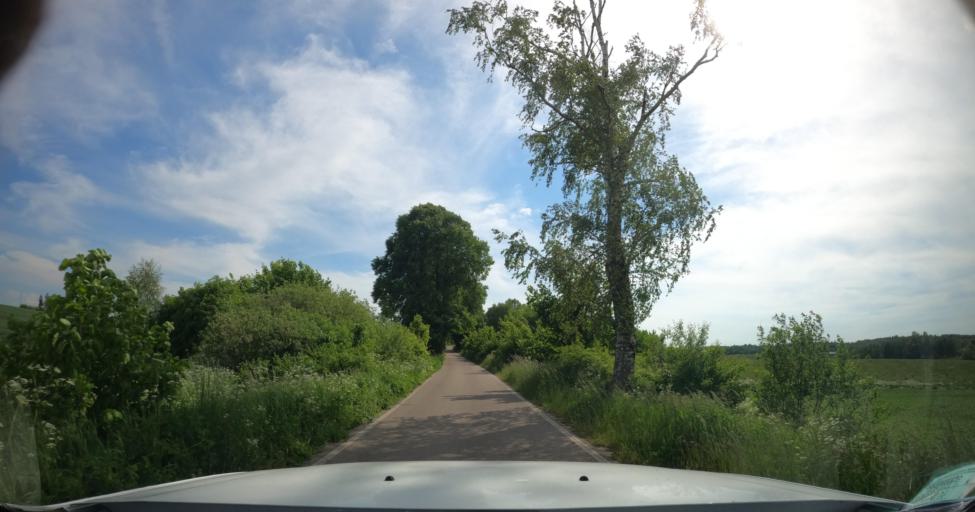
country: PL
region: Warmian-Masurian Voivodeship
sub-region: Powiat ostrodzki
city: Milakowo
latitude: 54.0185
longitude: 20.1582
